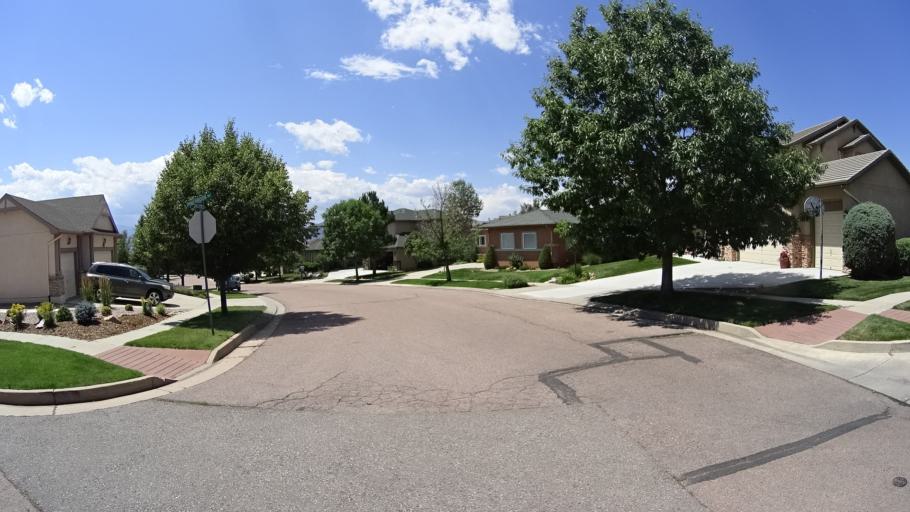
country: US
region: Colorado
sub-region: El Paso County
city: Black Forest
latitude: 38.9708
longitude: -104.7627
